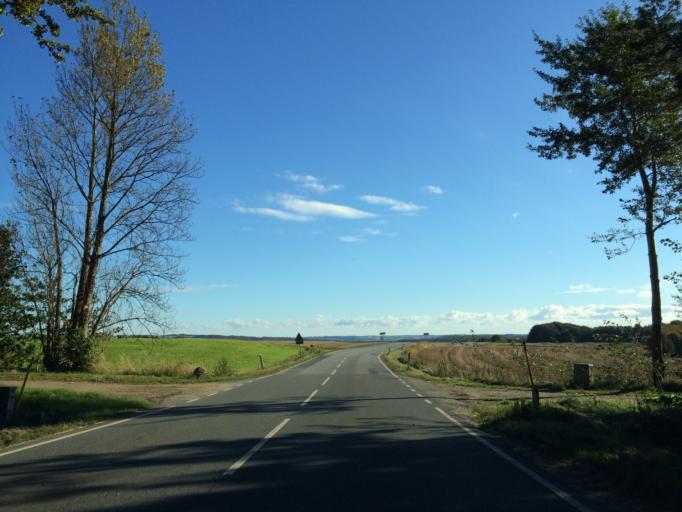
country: DK
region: Central Jutland
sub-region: Randers Kommune
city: Langa
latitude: 56.3459
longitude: 9.8759
